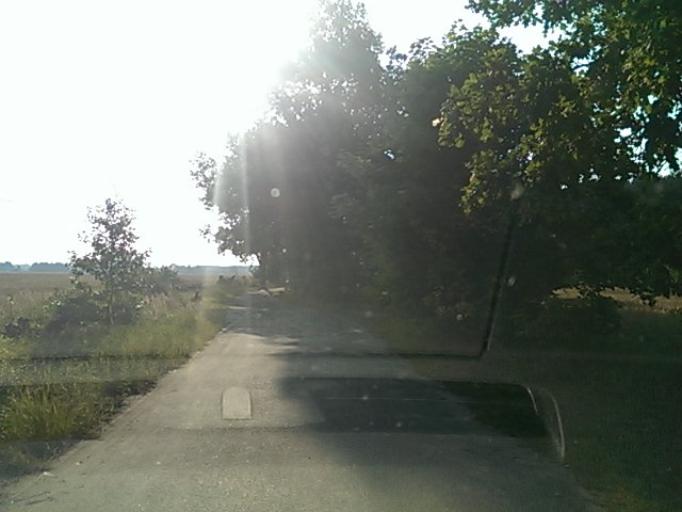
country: DE
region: Brandenburg
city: Trebbin
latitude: 52.2671
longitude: 13.1298
